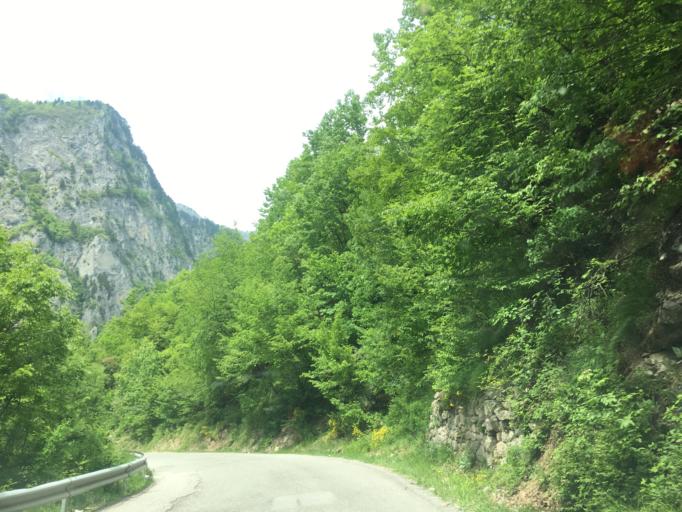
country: XK
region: Pec
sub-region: Komuna e Pejes
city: Peje
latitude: 42.6630
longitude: 20.2139
